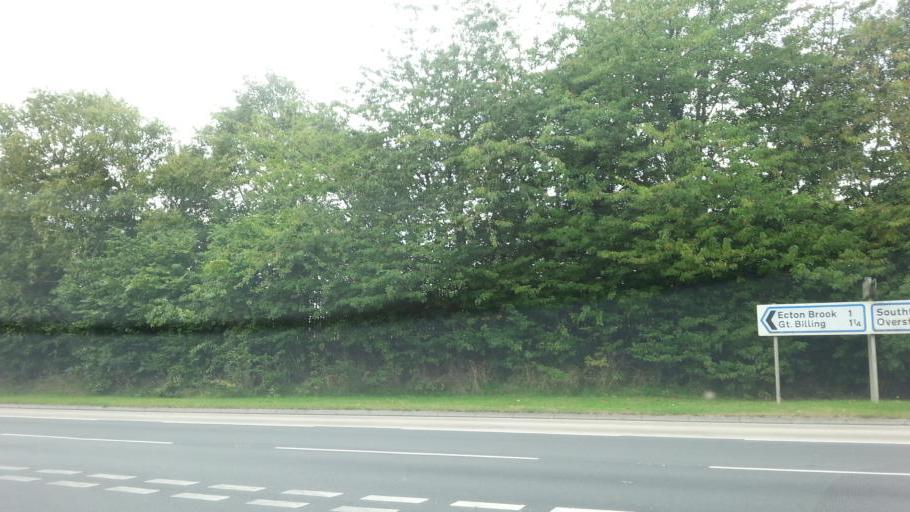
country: GB
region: England
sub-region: Northamptonshire
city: Earls Barton
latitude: 52.2700
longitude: -0.8124
